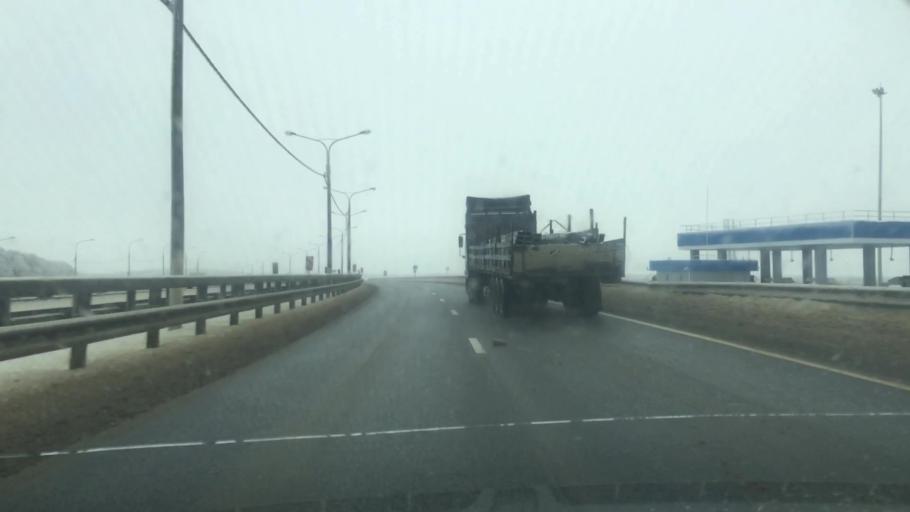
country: RU
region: Lipetsk
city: Yelets
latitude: 52.5437
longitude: 38.7209
